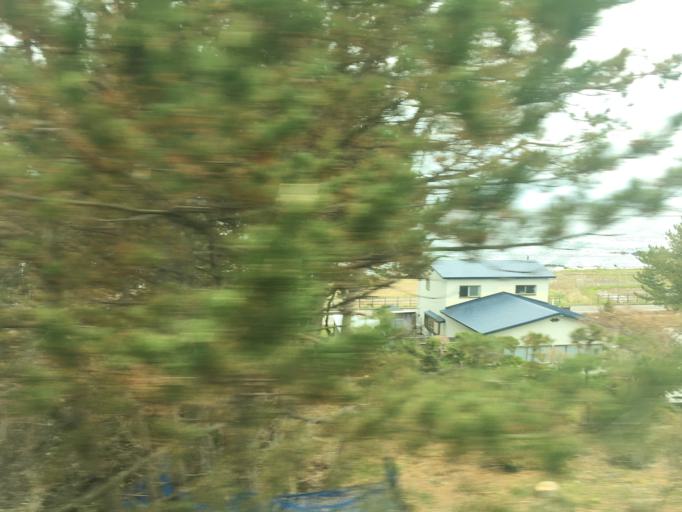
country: JP
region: Akita
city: Noshiromachi
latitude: 40.6244
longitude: 139.8806
